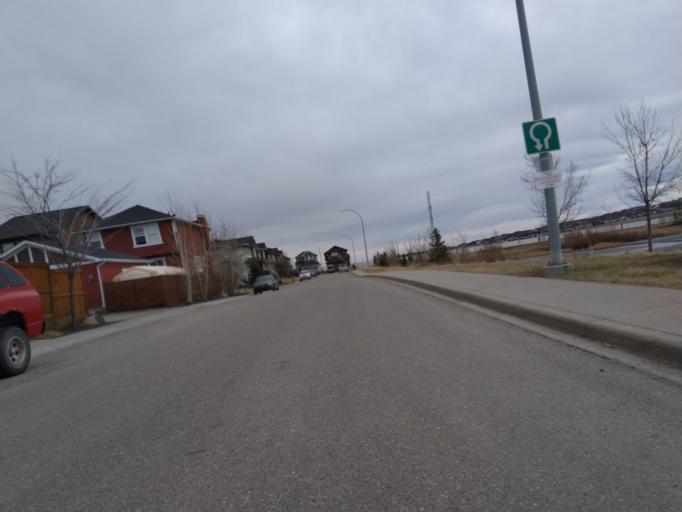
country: CA
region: Alberta
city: Calgary
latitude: 51.1750
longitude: -114.1030
